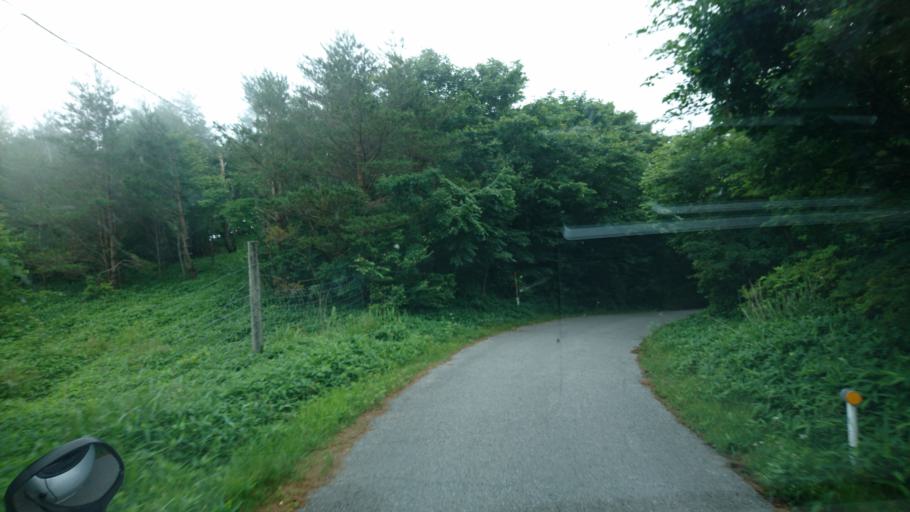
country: JP
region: Iwate
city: Ofunato
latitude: 39.1435
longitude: 141.7538
